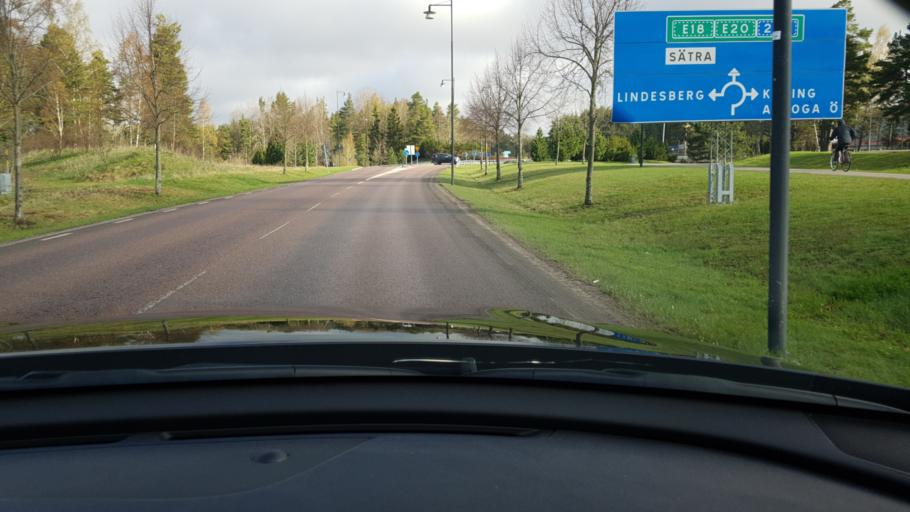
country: SE
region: Vaestmanland
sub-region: Arboga Kommun
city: Arboga
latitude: 59.4033
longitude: 15.8319
